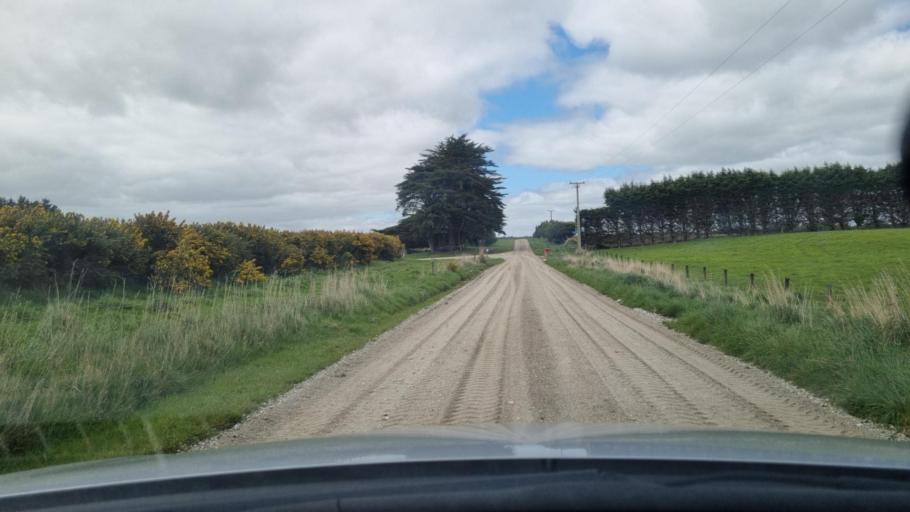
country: NZ
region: Southland
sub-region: Invercargill City
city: Invercargill
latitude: -46.4342
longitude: 168.4085
